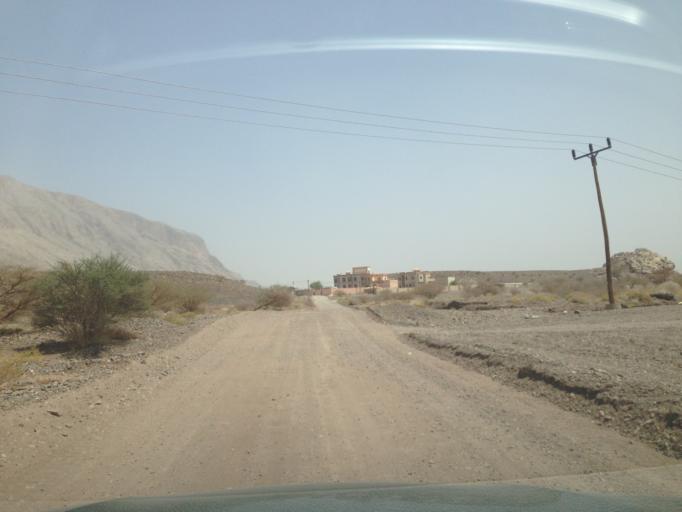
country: OM
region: Az Zahirah
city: `Ibri
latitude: 23.1754
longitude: 56.9017
